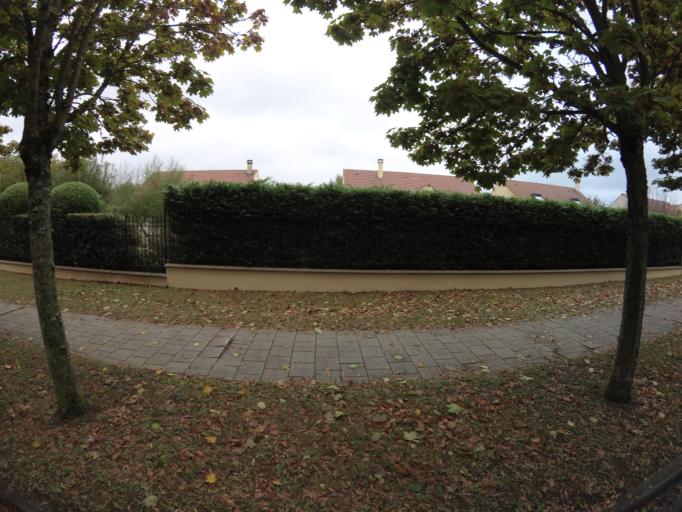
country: FR
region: Ile-de-France
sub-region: Departement de Seine-et-Marne
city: Chanteloup-en-Brie
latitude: 48.8466
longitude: 2.7318
